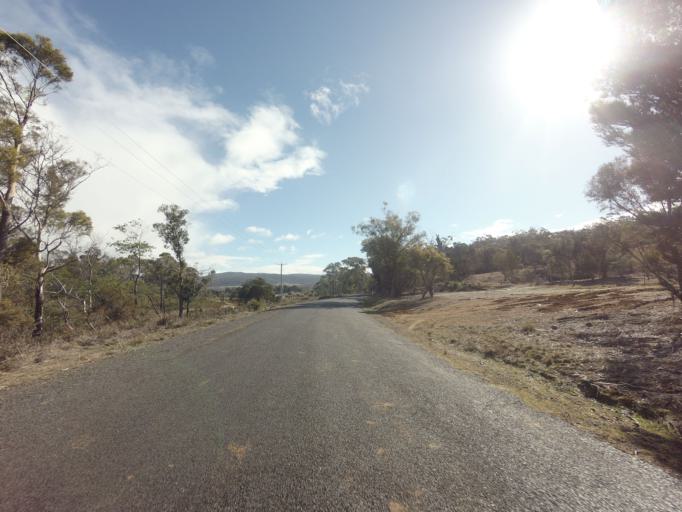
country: AU
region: Tasmania
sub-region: Sorell
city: Sorell
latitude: -42.3623
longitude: 147.9483
